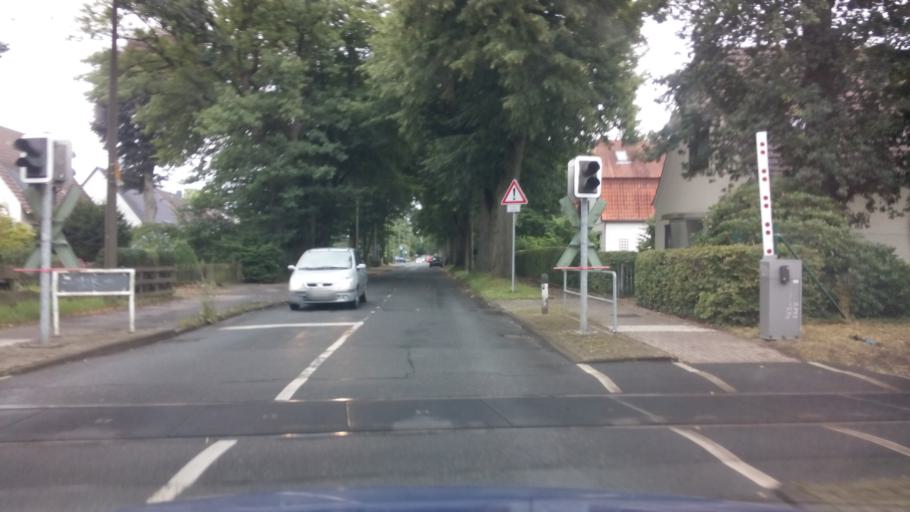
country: DE
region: Lower Saxony
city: Lemwerder
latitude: 53.1802
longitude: 8.6309
